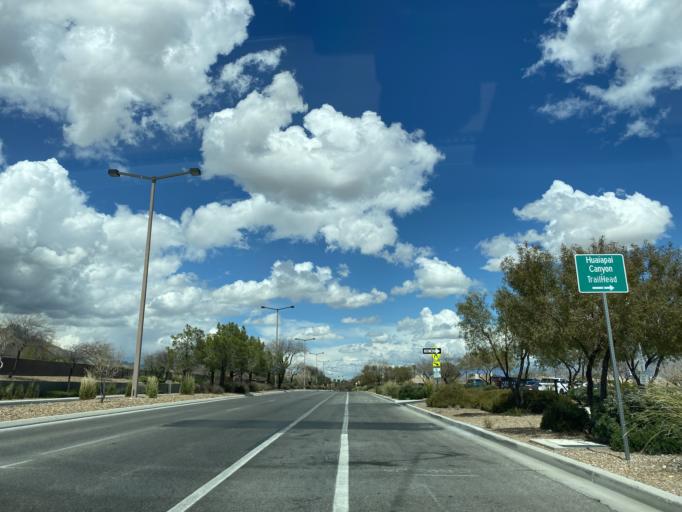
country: US
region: Nevada
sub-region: Clark County
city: Summerlin South
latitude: 36.1721
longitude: -115.3157
